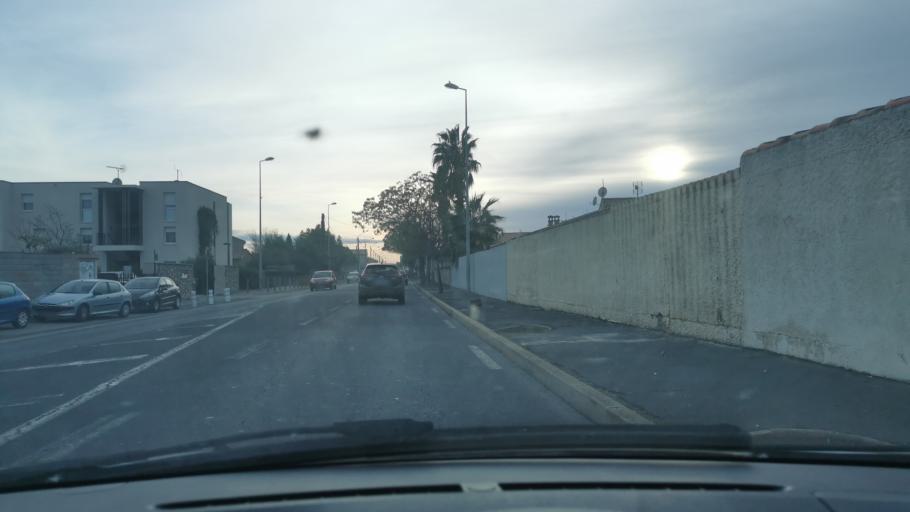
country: FR
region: Languedoc-Roussillon
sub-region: Departement de l'Herault
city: Frontignan
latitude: 43.4591
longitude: 3.7639
